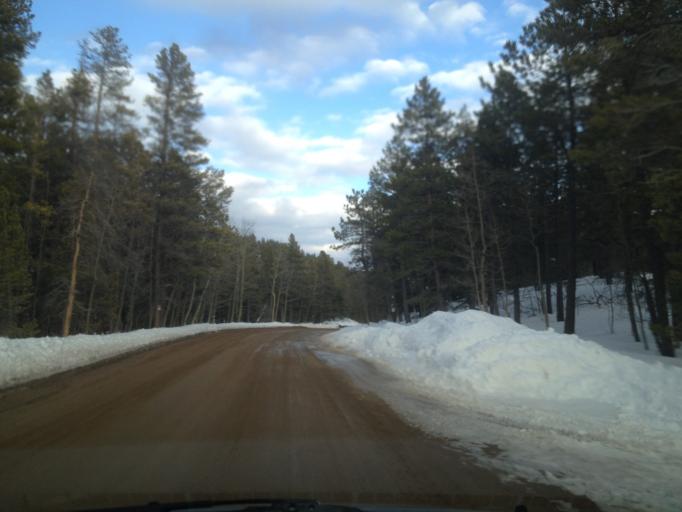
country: US
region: Colorado
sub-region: Boulder County
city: Nederland
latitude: 40.1259
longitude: -105.4701
